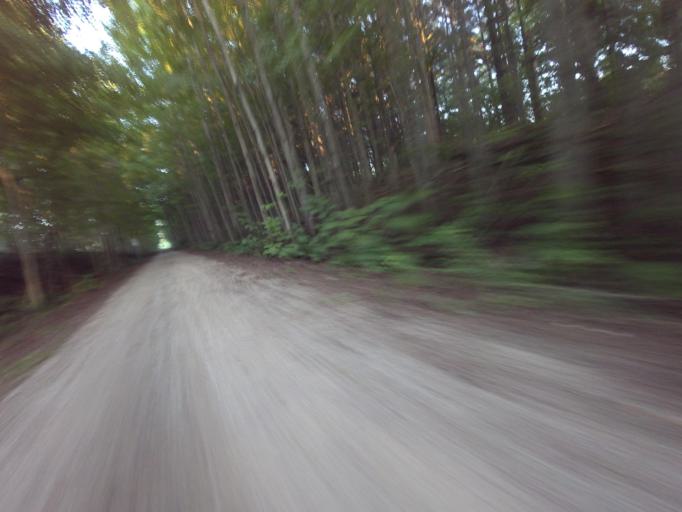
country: CA
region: Ontario
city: Goderich
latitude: 43.7493
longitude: -81.6531
